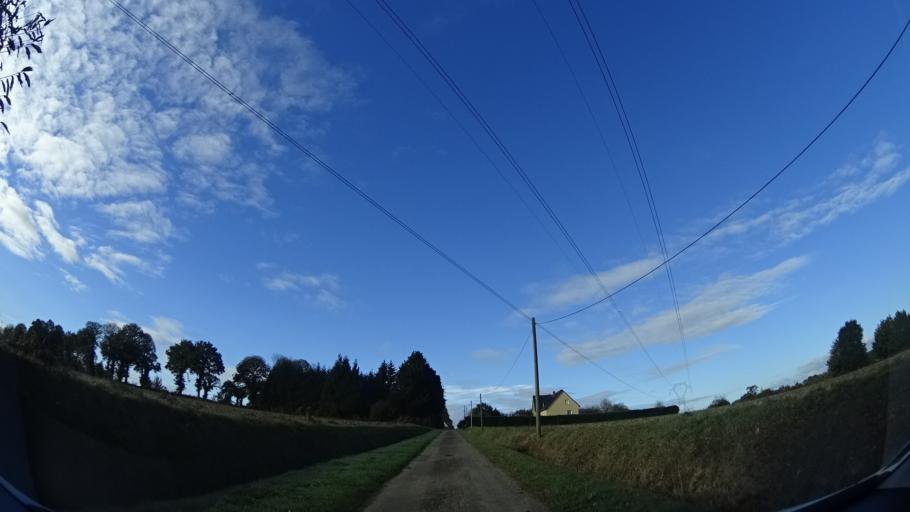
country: FR
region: Brittany
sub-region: Departement d'Ille-et-Vilaine
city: Geveze
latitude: 48.1976
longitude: -1.7891
